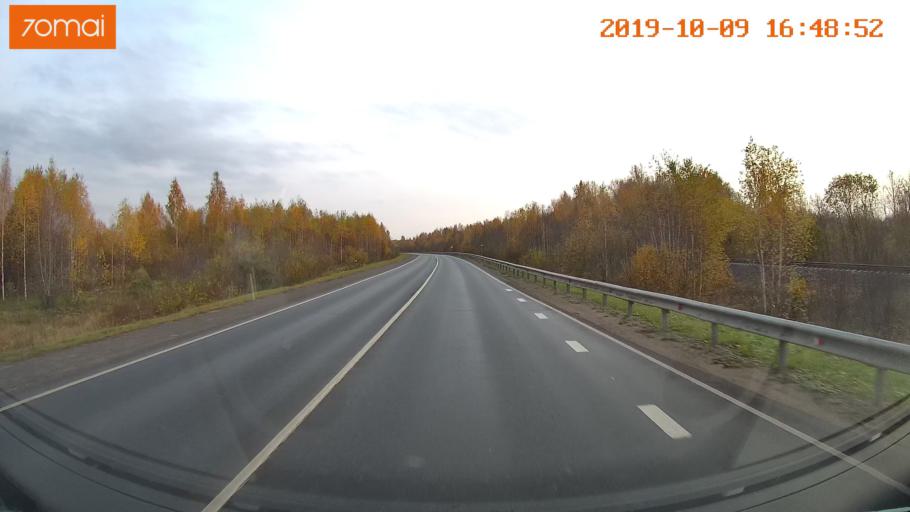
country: RU
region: Kostroma
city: Volgorechensk
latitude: 57.4230
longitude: 41.1909
